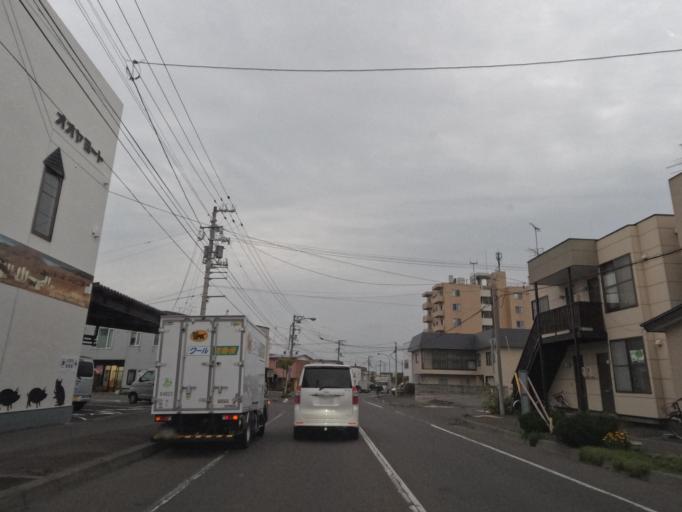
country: JP
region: Hokkaido
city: Date
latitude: 42.4709
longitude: 140.8571
